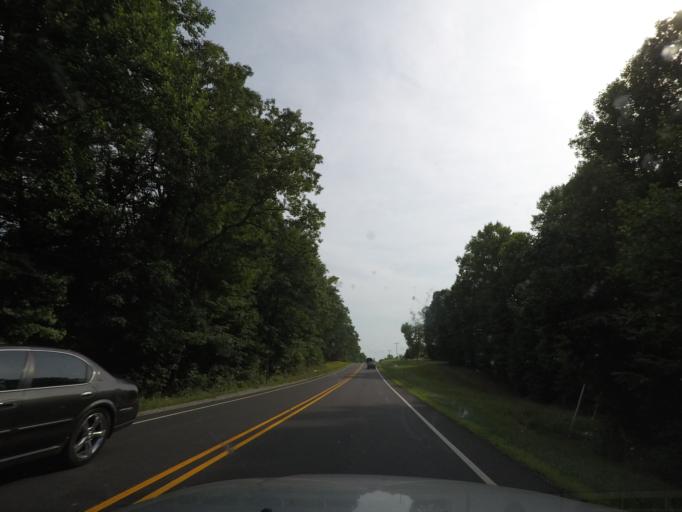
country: US
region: Virginia
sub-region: Prince Edward County
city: Hampden Sydney
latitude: 37.1232
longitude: -78.4534
